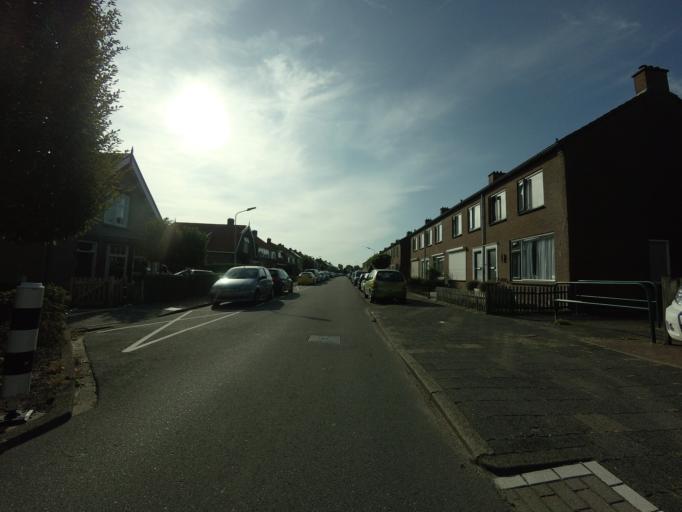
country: NL
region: Utrecht
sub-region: Gemeente Lopik
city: Lopik
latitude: 51.9536
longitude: 4.9634
